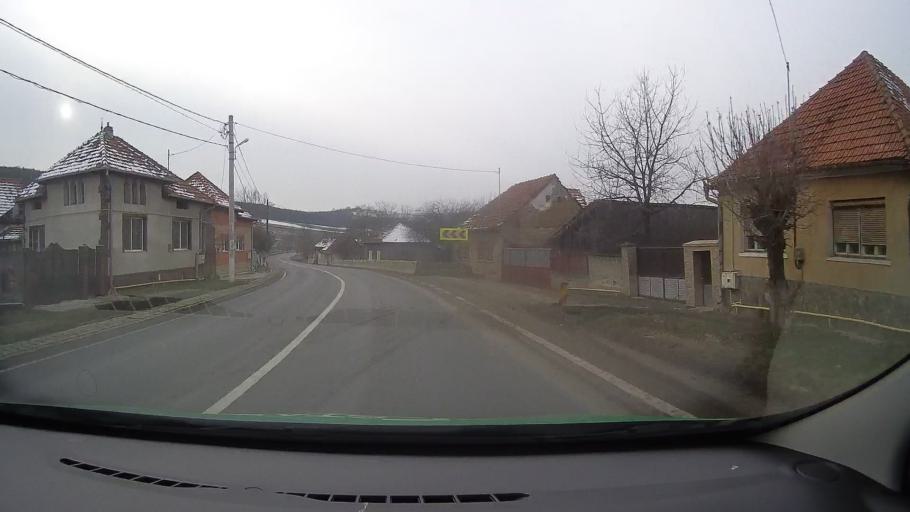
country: RO
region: Hunedoara
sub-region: Comuna Turdas
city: Turdas
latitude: 45.8335
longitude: 23.0853
